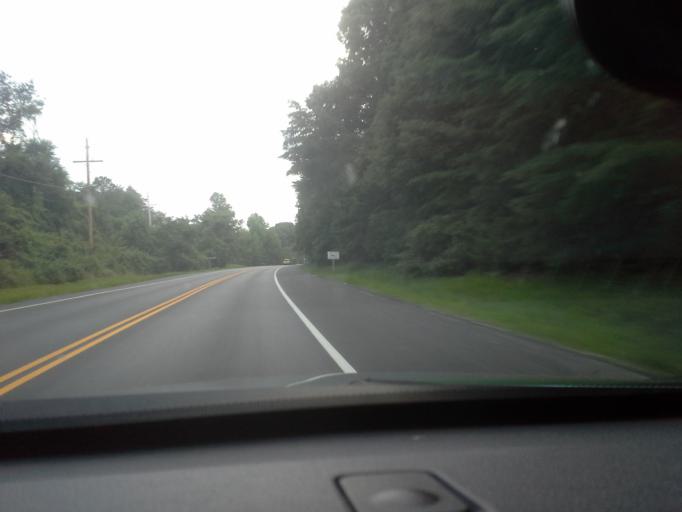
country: US
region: Maryland
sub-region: Calvert County
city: Prince Frederick
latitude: 38.5530
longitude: -76.5635
